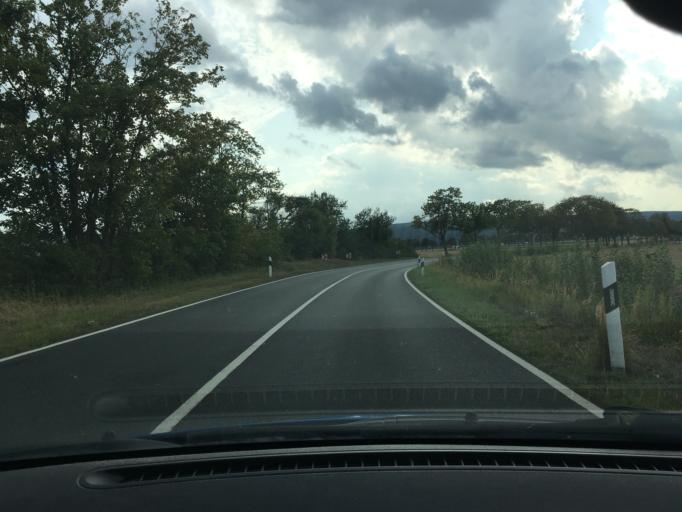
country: DE
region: Lower Saxony
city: Egestorf
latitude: 52.3023
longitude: 9.5214
